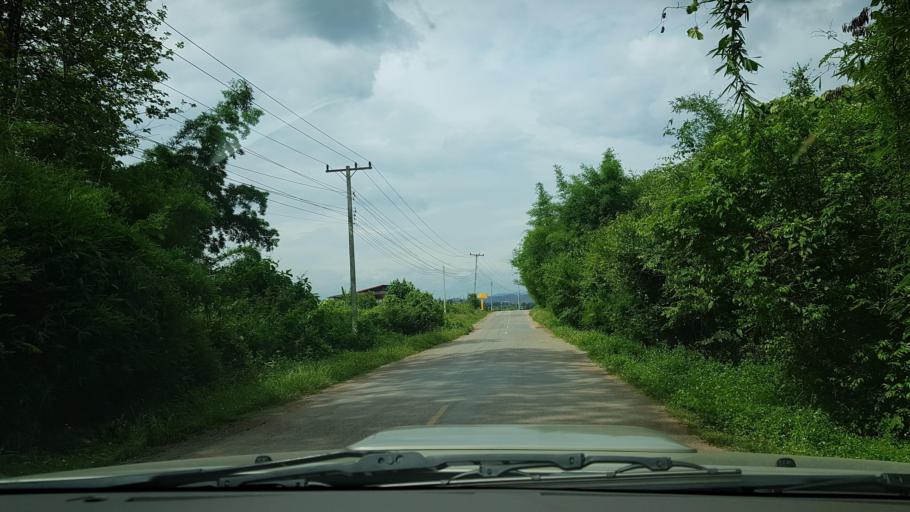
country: LA
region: Loungnamtha
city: Muang Nale
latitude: 20.3129
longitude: 101.6528
